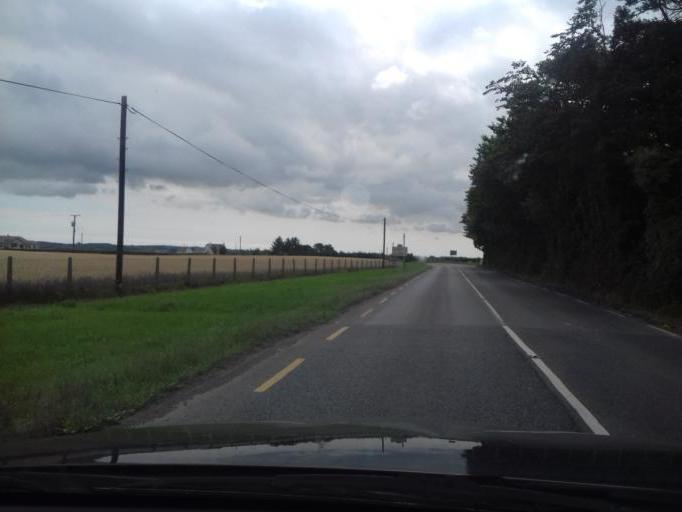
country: IE
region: Leinster
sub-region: Loch Garman
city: Ballinroad
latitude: 52.4721
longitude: -6.3991
